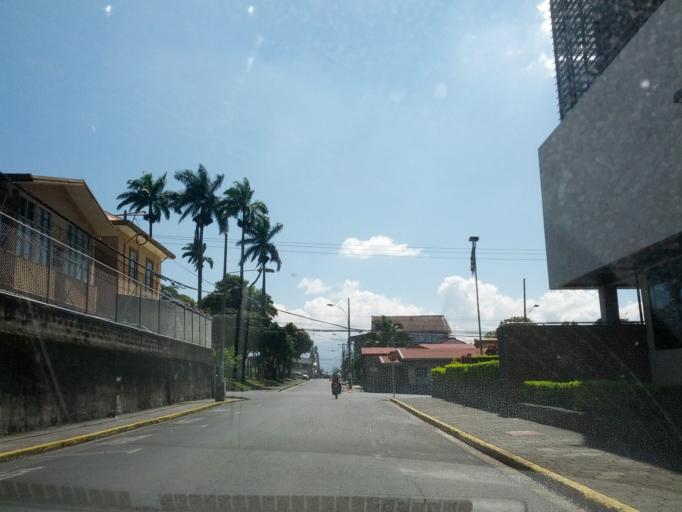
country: CR
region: Alajuela
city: Alajuela
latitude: 10.0209
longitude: -84.2147
